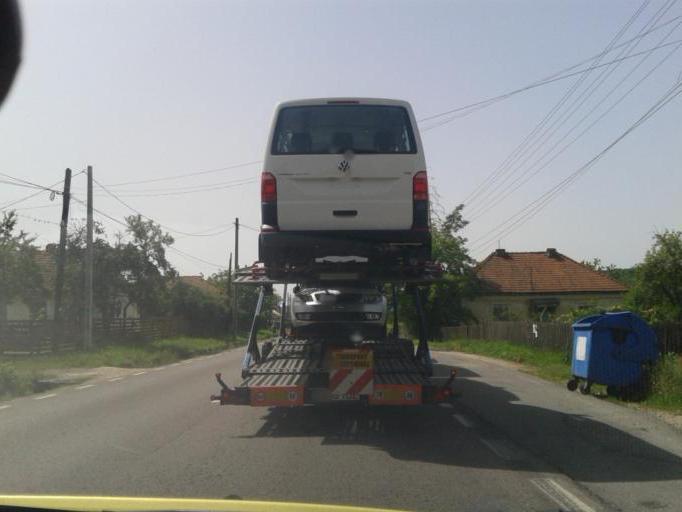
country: RO
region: Arges
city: Draganu-Olteni
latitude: 44.9558
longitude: 24.6951
